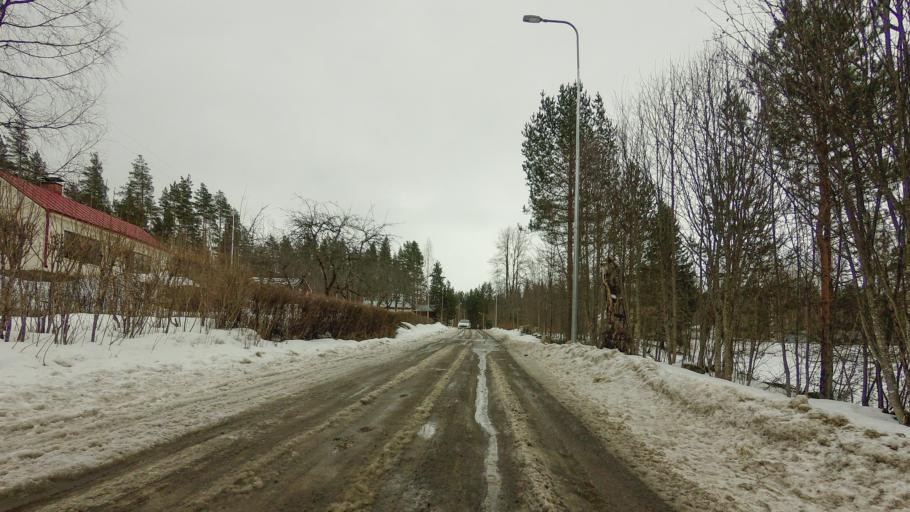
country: FI
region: Southern Savonia
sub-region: Savonlinna
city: Rantasalmi
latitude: 62.1122
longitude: 28.6094
